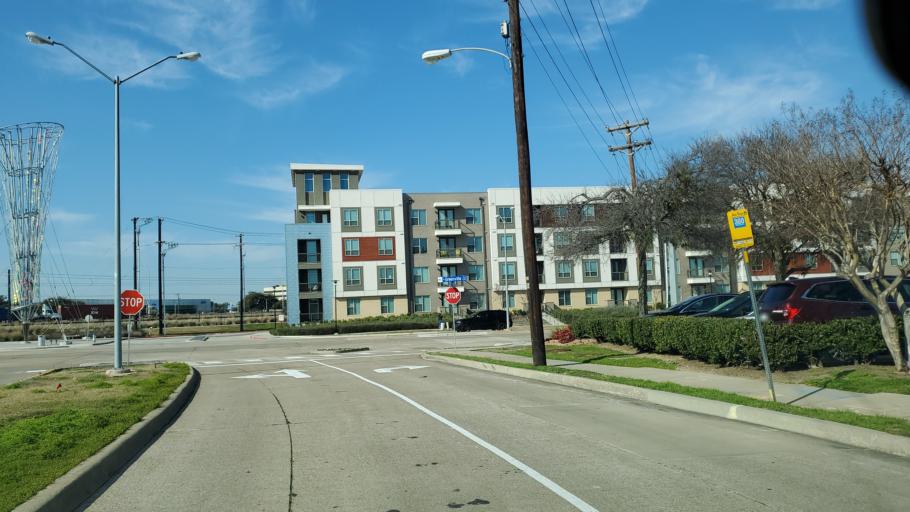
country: US
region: Texas
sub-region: Dallas County
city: Richardson
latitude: 32.9706
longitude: -96.7171
